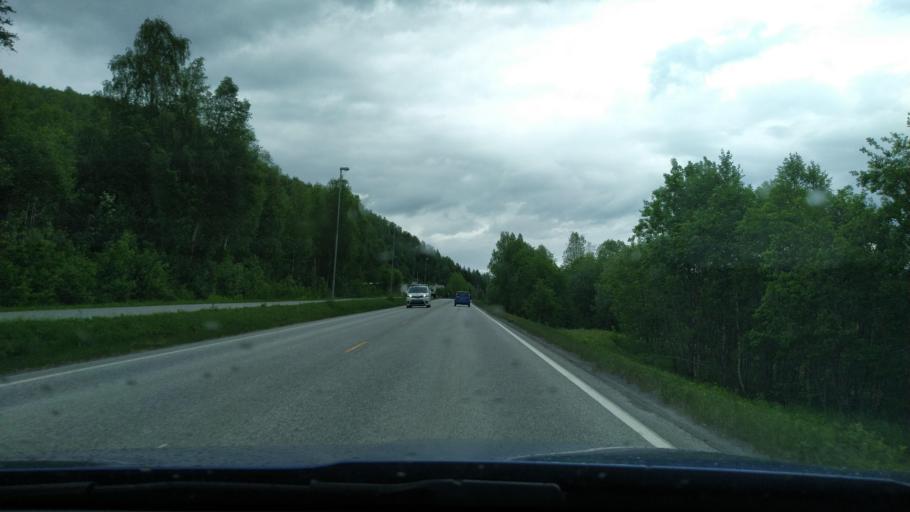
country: NO
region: Troms
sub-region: Malselv
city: Moen
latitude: 69.0212
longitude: 18.4894
